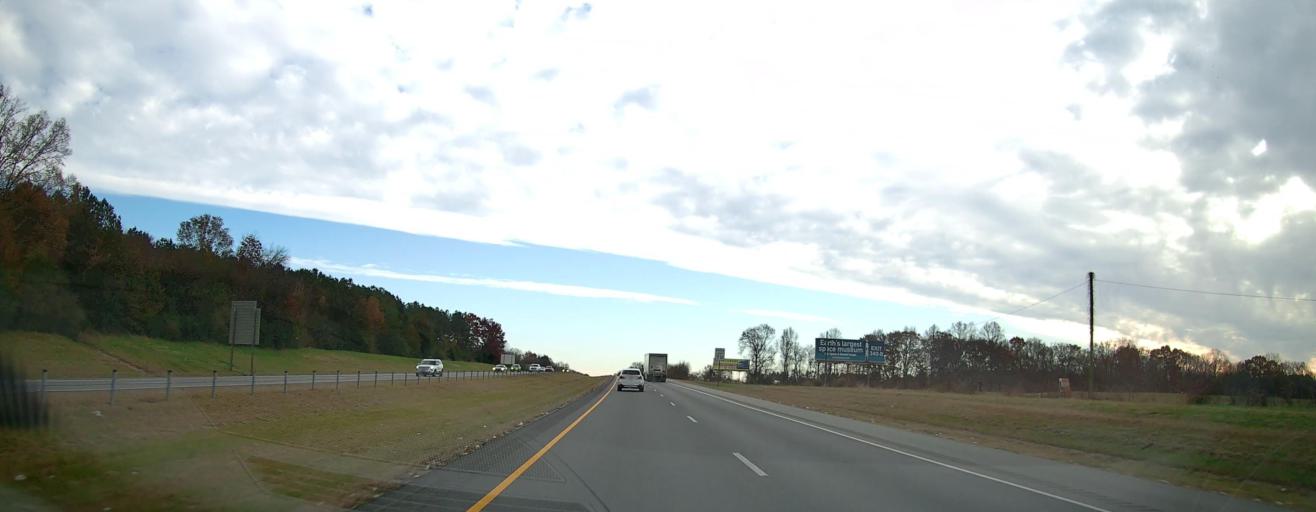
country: US
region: Alabama
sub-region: Limestone County
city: Athens
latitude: 34.7735
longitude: -86.9400
